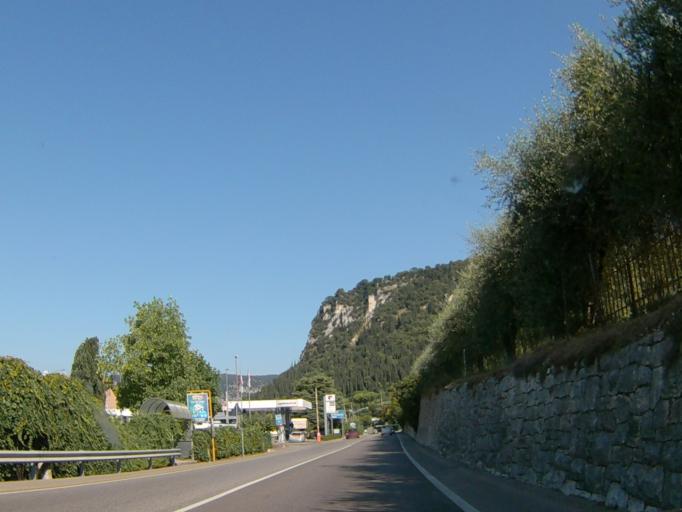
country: IT
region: Veneto
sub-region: Provincia di Verona
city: Garda
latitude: 45.5616
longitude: 10.7154
